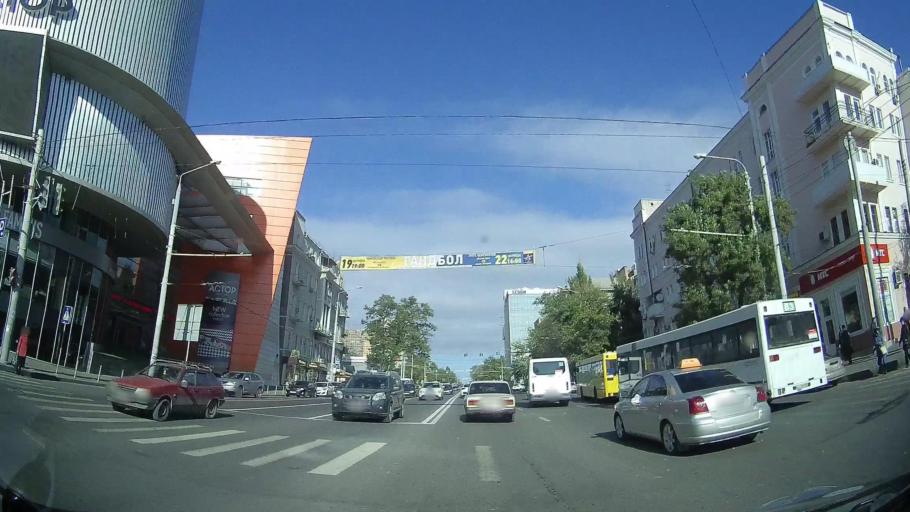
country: RU
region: Rostov
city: Rostov-na-Donu
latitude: 47.2247
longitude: 39.7057
